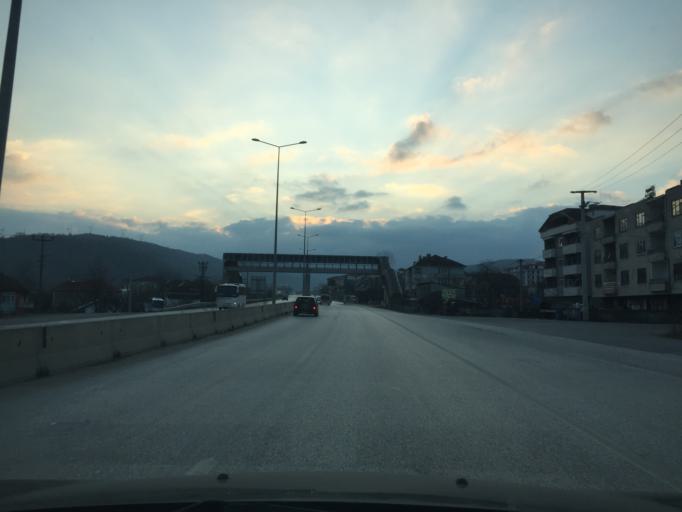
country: TR
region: Duzce
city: Gumusova
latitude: 40.8517
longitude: 30.9500
